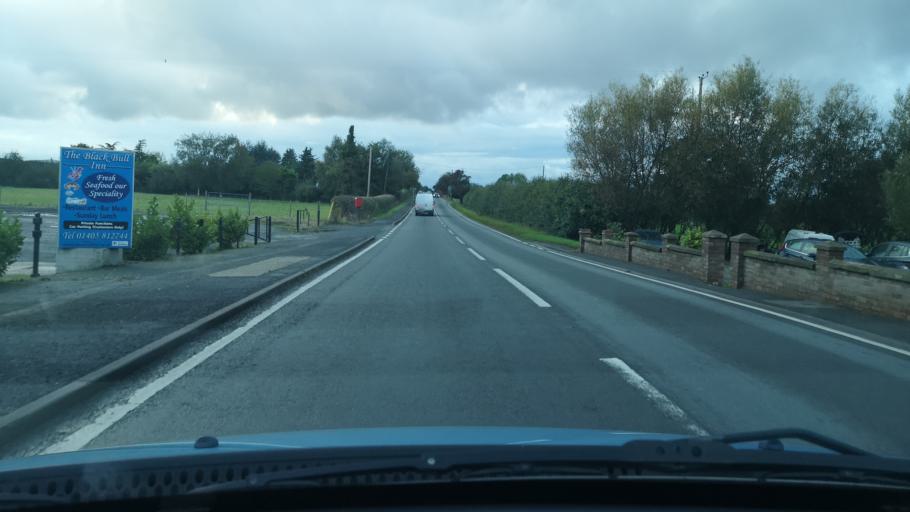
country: GB
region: England
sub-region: Doncaster
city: Hatfield
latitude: 53.5875
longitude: -0.9180
